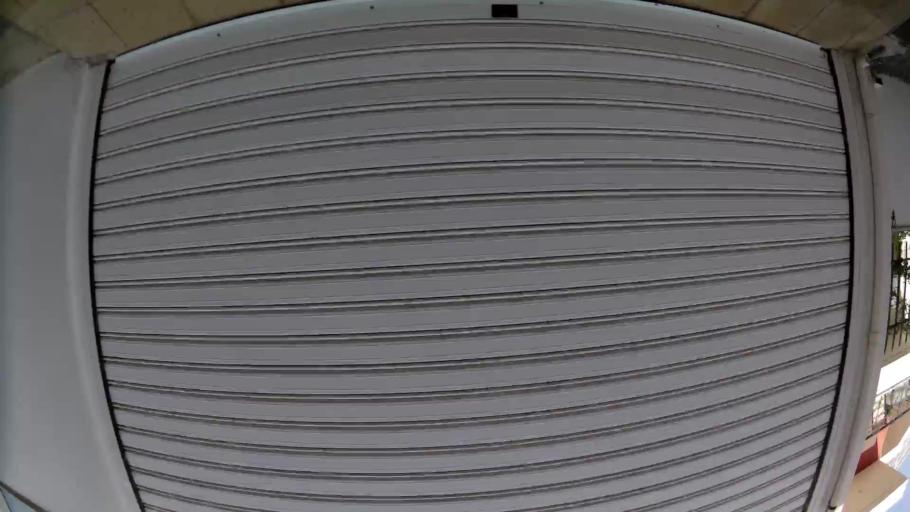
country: GR
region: Attica
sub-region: Nomarchia Athinas
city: Kamateron
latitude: 38.0558
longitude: 23.7074
